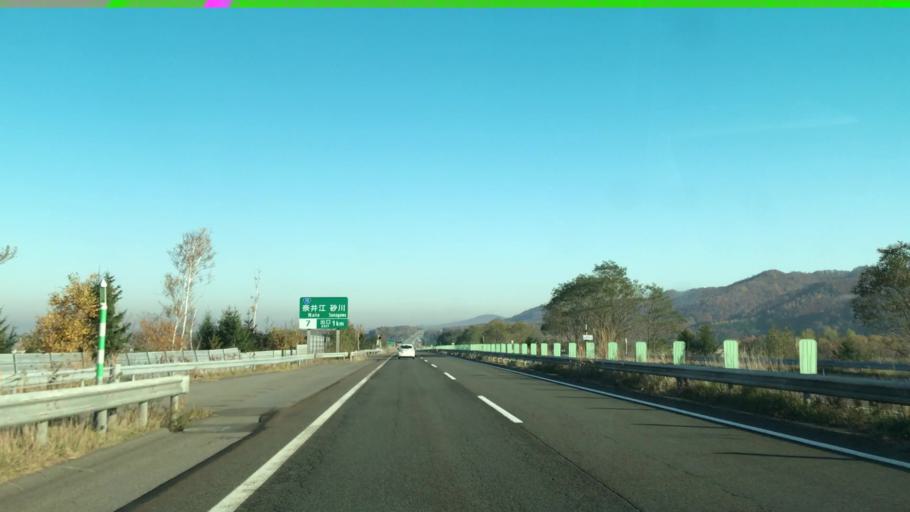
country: JP
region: Hokkaido
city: Sunagawa
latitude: 43.4391
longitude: 141.9160
